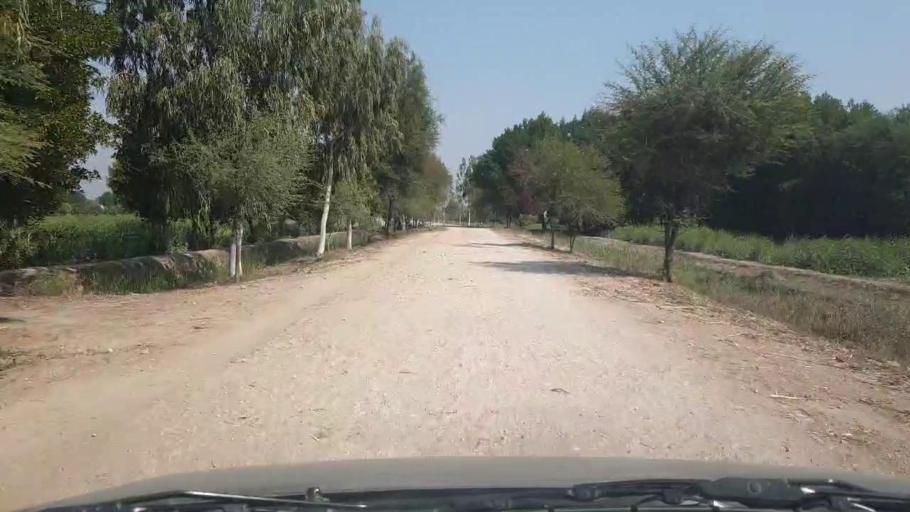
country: PK
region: Sindh
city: Mirwah Gorchani
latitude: 25.3502
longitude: 69.1426
